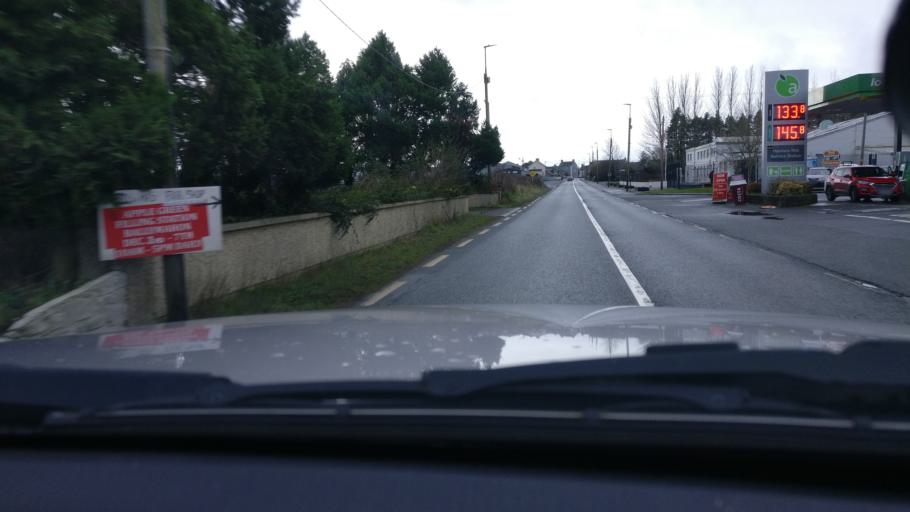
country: IE
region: Leinster
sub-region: An Longfort
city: Ballymahon
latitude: 53.5680
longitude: -7.7605
